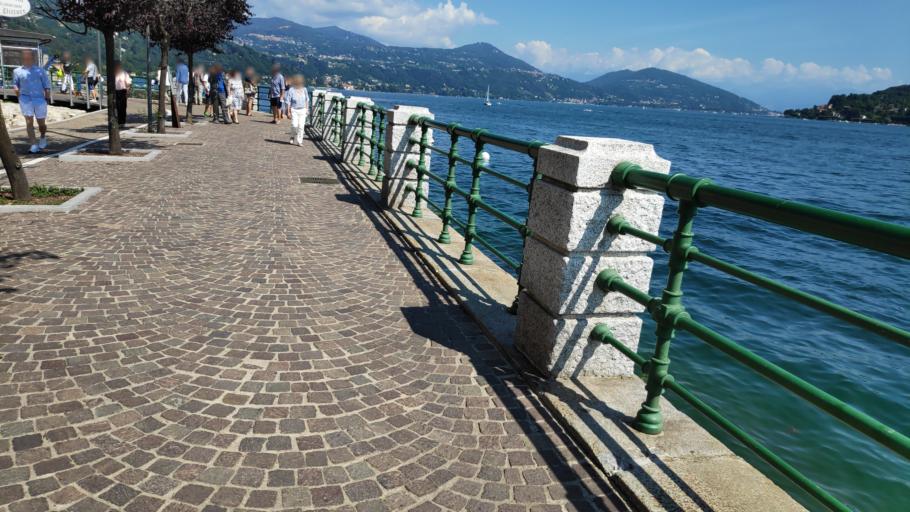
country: IT
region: Piedmont
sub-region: Provincia di Novara
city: Arona
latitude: 45.7630
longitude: 8.5603
